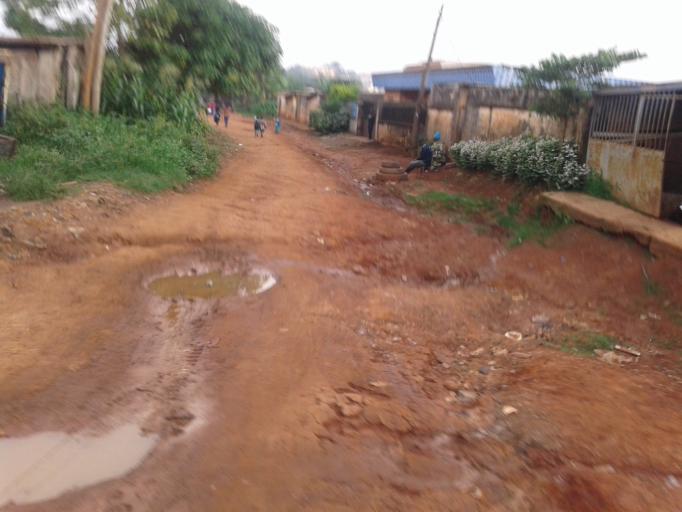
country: CM
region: Centre
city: Yaounde
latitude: 3.9081
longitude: 11.5298
